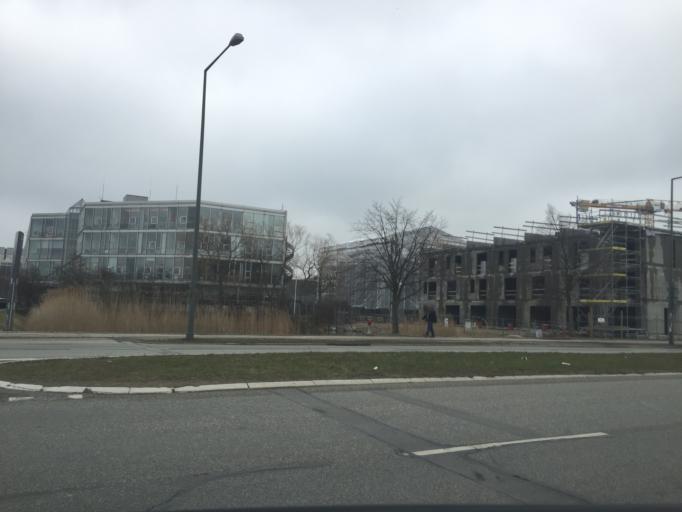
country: DK
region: Capital Region
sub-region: Tarnby Kommune
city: Tarnby
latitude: 55.6382
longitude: 12.5746
